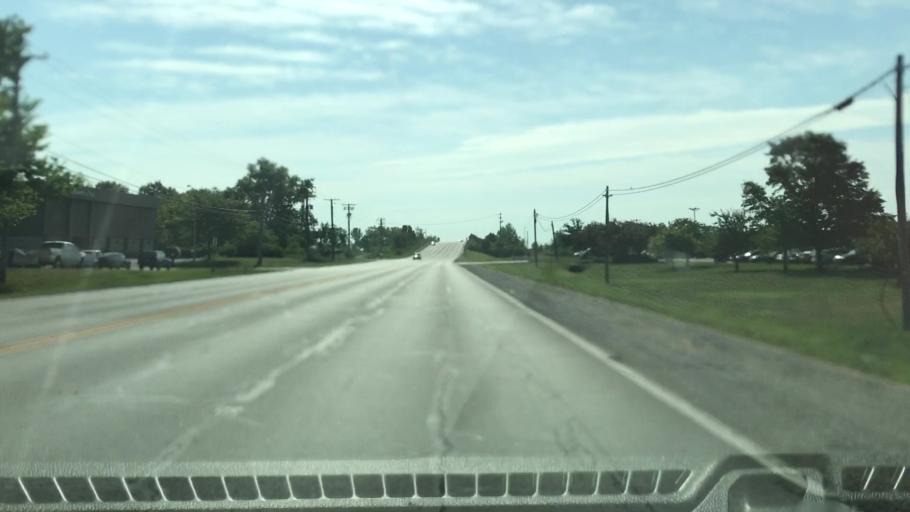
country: US
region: Ohio
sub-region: Franklin County
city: Lincoln Village
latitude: 39.9736
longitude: -83.1363
